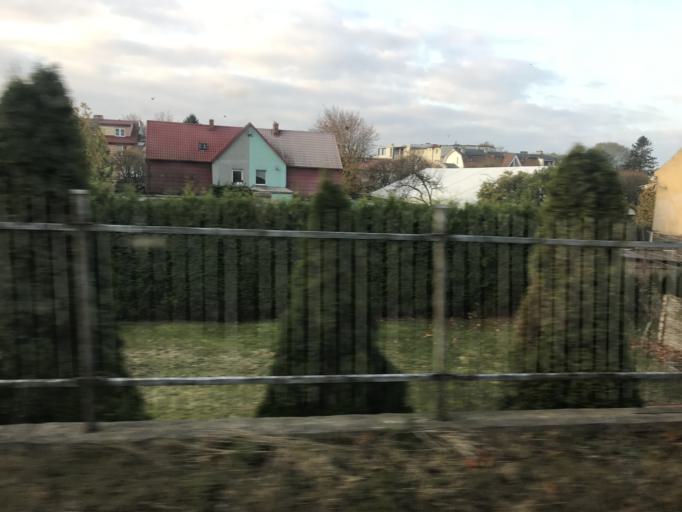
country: PL
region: Pomeranian Voivodeship
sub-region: Powiat pucki
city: Jastarnia
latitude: 54.7004
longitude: 18.6787
